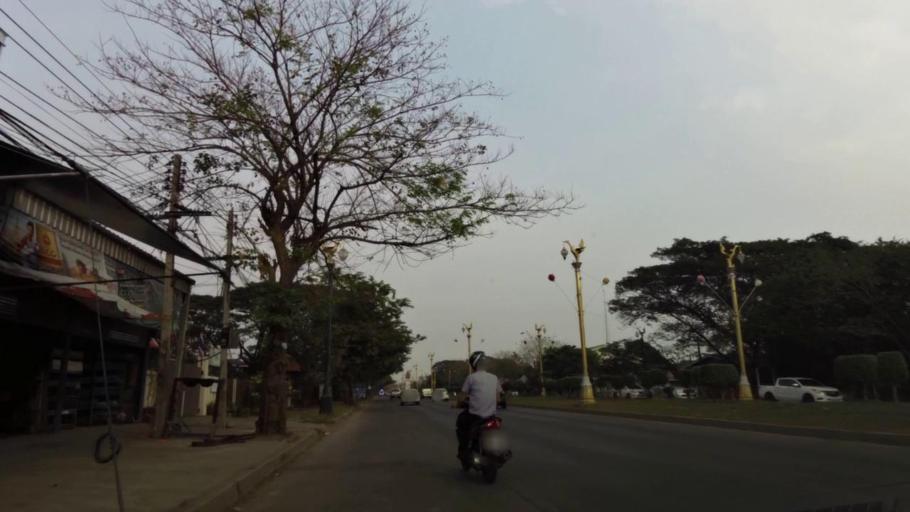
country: TH
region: Phra Nakhon Si Ayutthaya
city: Phra Nakhon Si Ayutthaya
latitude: 14.3511
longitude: 100.5720
